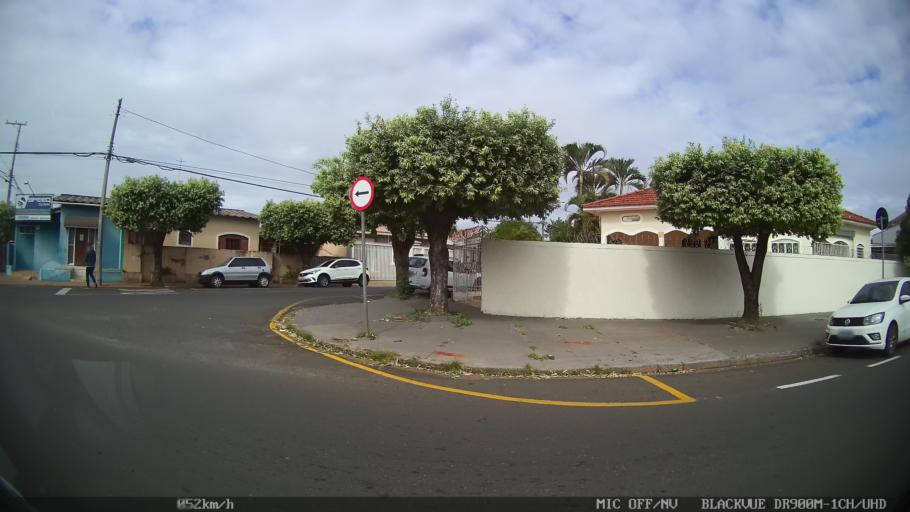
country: BR
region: Sao Paulo
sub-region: Sao Jose Do Rio Preto
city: Sao Jose do Rio Preto
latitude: -20.8171
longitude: -49.3608
